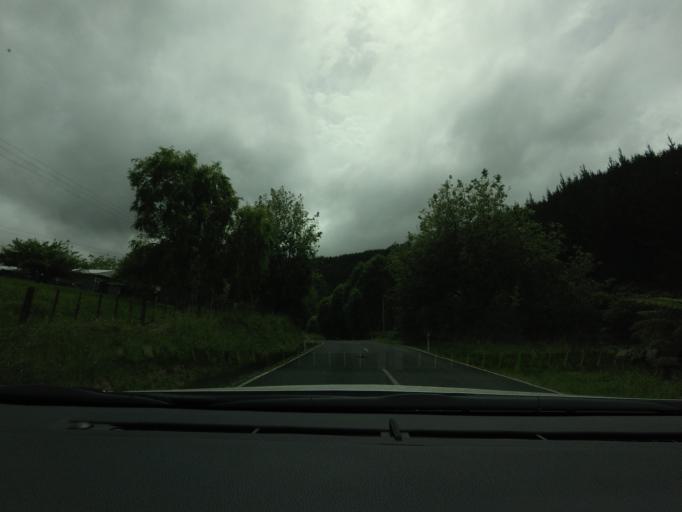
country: NZ
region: Auckland
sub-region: Auckland
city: Warkworth
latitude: -36.4969
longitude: 174.6272
